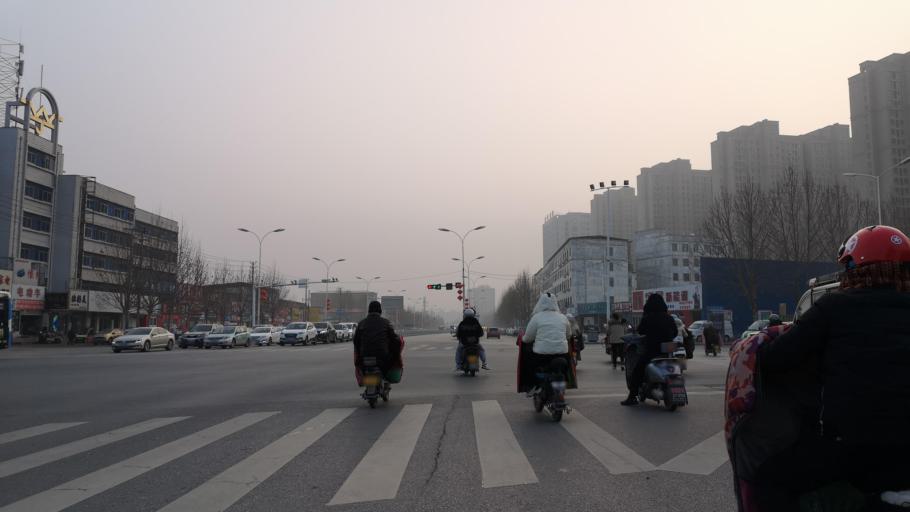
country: CN
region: Henan Sheng
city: Puyang
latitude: 35.7491
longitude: 115.0290
